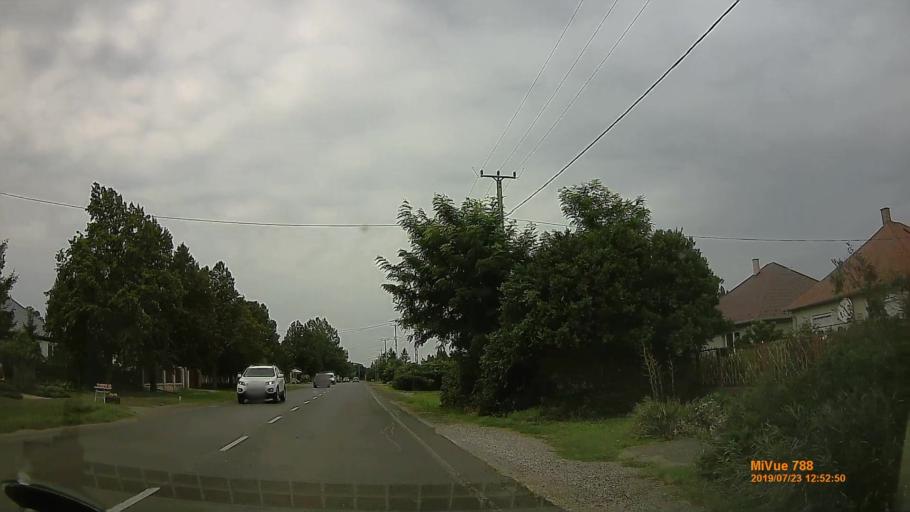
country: HU
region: Szabolcs-Szatmar-Bereg
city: Nagycserkesz
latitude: 47.9623
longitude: 21.5616
